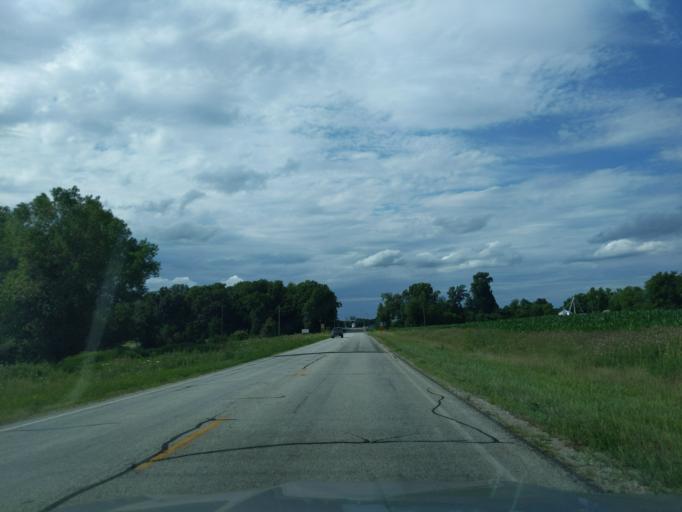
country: US
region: Indiana
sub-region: Ripley County
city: Sunman
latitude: 39.2763
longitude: -85.0987
